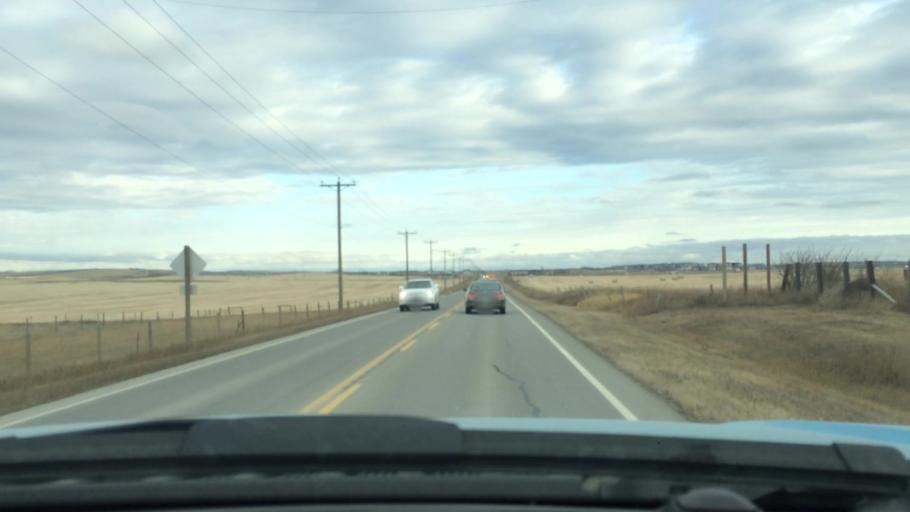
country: CA
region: Alberta
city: Airdrie
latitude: 51.2340
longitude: -114.0249
